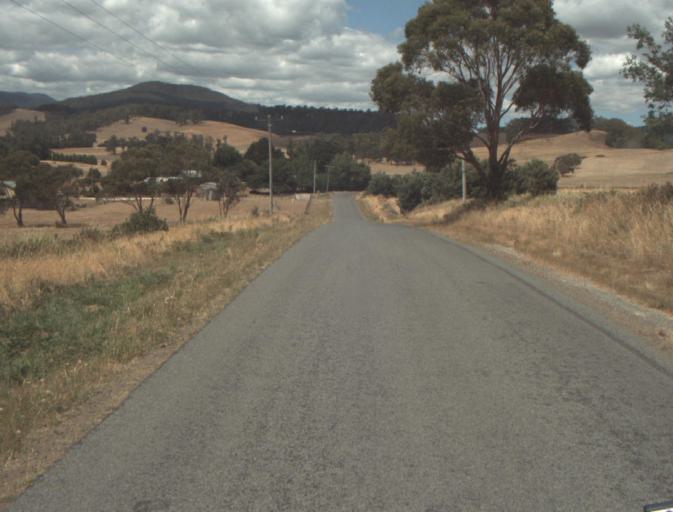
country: AU
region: Tasmania
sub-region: Launceston
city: Mayfield
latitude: -41.2337
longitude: 147.1477
